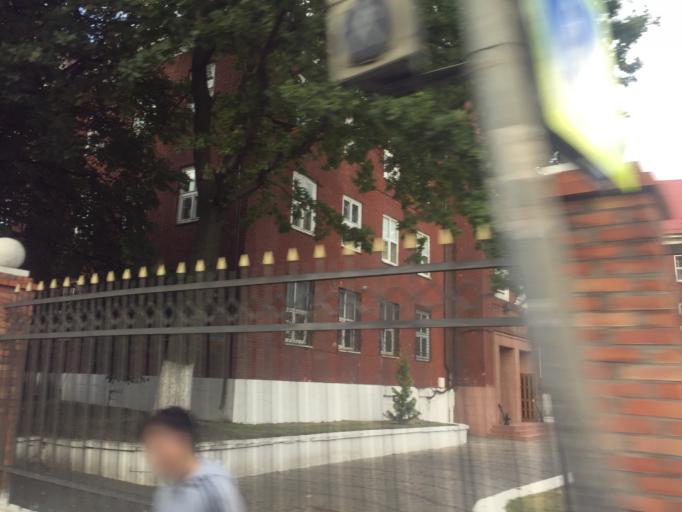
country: RU
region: Kaliningrad
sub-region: Gorod Kaliningrad
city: Kaliningrad
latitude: 54.7336
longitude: 20.4851
